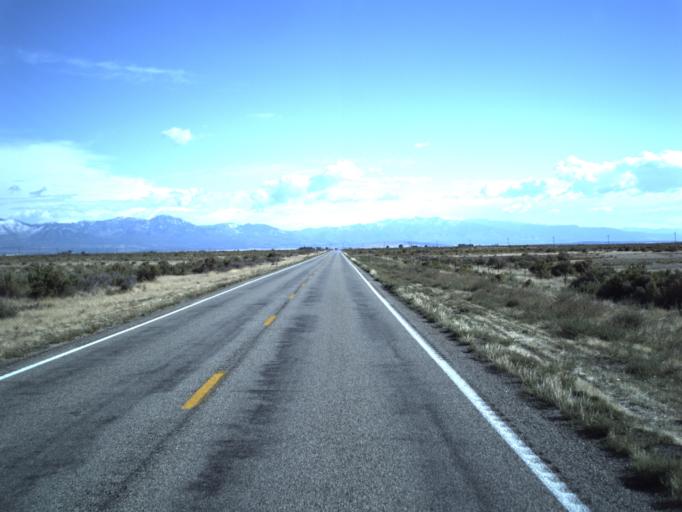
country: US
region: Utah
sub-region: Millard County
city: Delta
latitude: 39.2426
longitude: -112.4345
